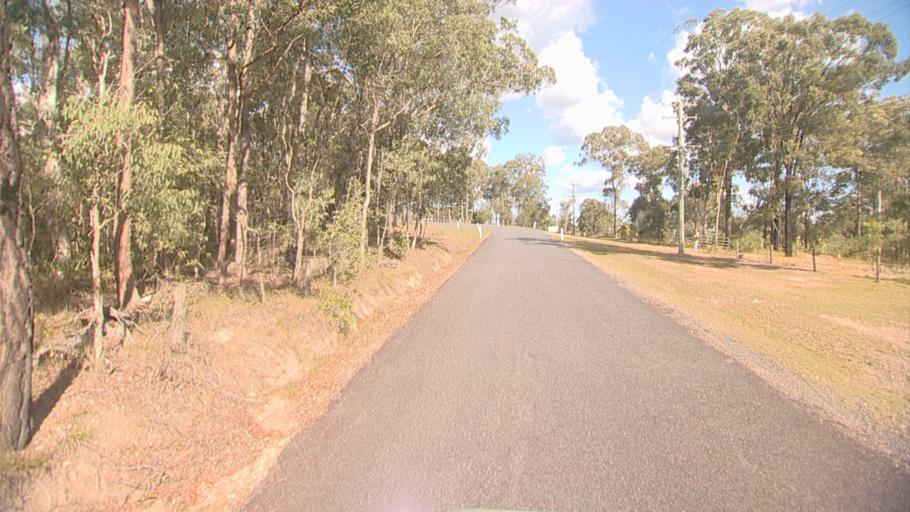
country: AU
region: Queensland
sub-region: Logan
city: Beenleigh
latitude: -27.6505
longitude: 153.2278
